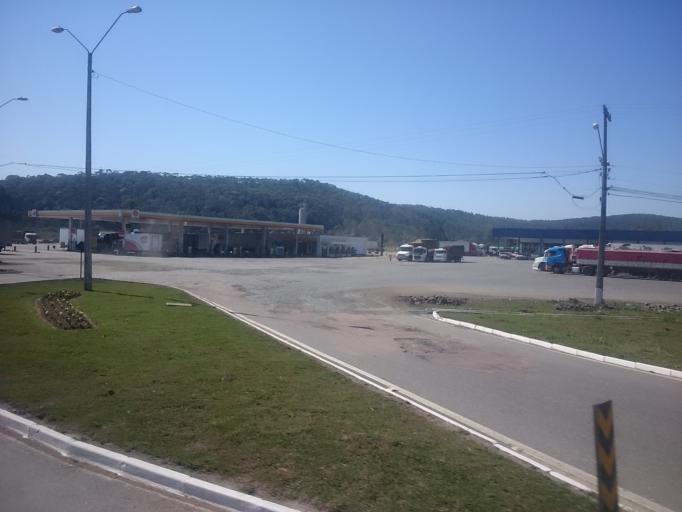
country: BR
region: Santa Catarina
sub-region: Santa Cecilia
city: Santa Cecilia
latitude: -26.7055
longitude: -50.2925
